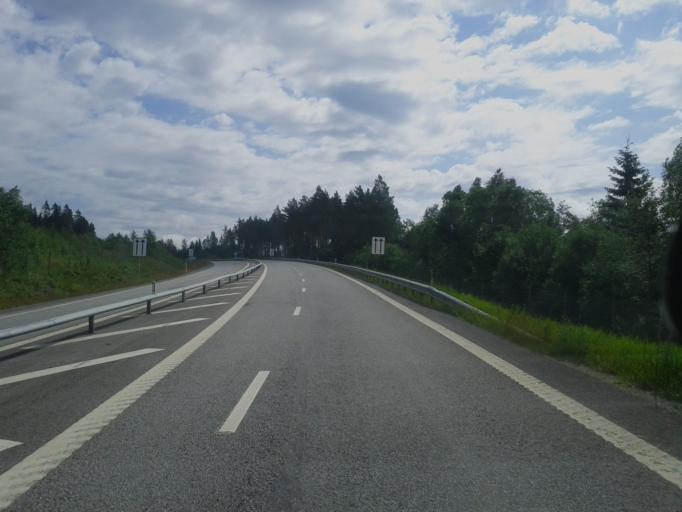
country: SE
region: Vaesternorrland
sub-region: OErnskoeldsviks Kommun
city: Ornskoldsvik
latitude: 63.2974
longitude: 18.8701
